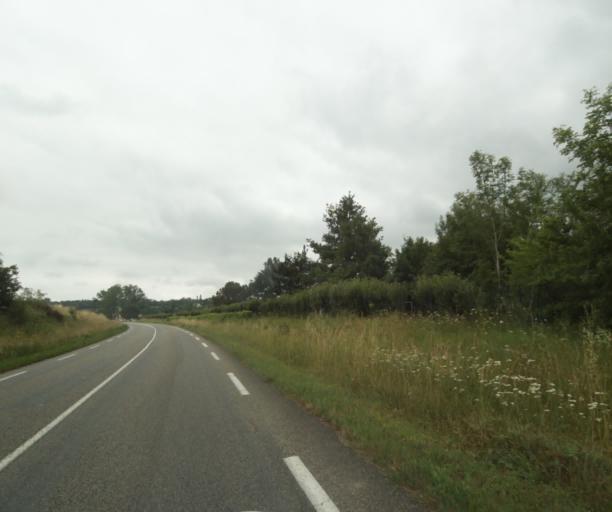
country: FR
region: Midi-Pyrenees
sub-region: Departement du Tarn-et-Garonne
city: Saint-Nauphary
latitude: 43.9830
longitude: 1.3931
